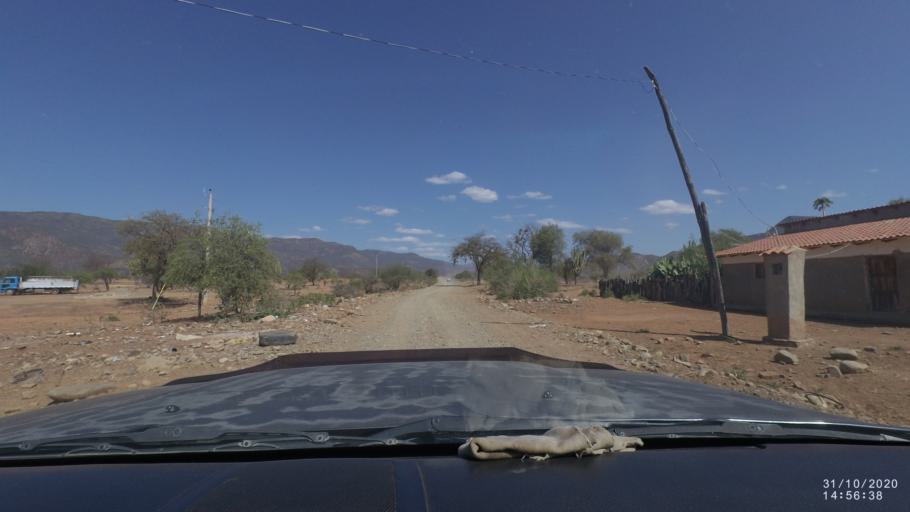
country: BO
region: Cochabamba
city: Aiquile
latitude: -18.2395
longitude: -64.8490
